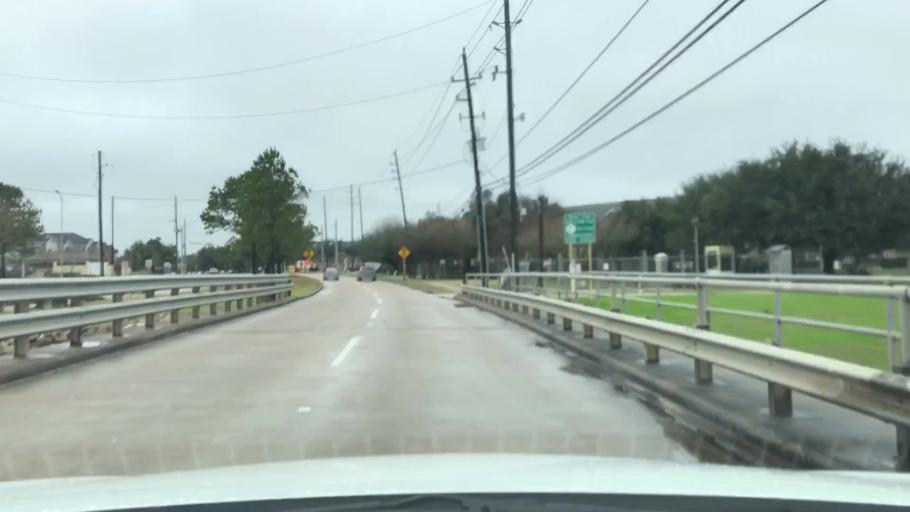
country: US
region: Texas
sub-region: Fort Bend County
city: Cinco Ranch
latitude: 29.7763
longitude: -95.7376
